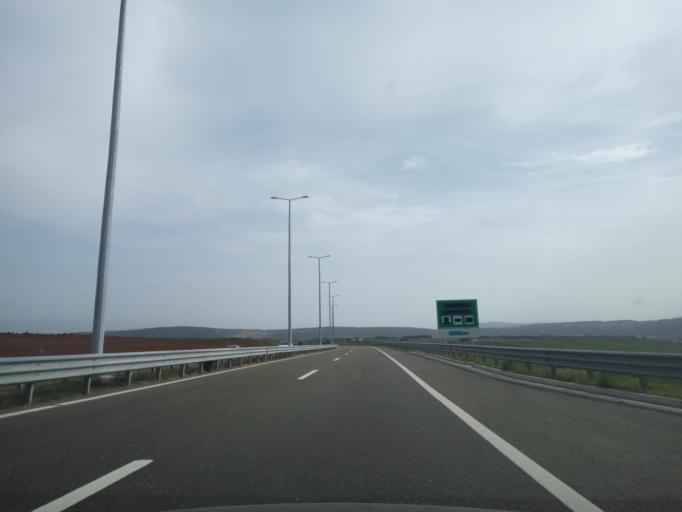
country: XK
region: Prizren
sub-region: Komuna e Malisheves
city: Malisevo
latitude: 42.4925
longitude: 20.7943
